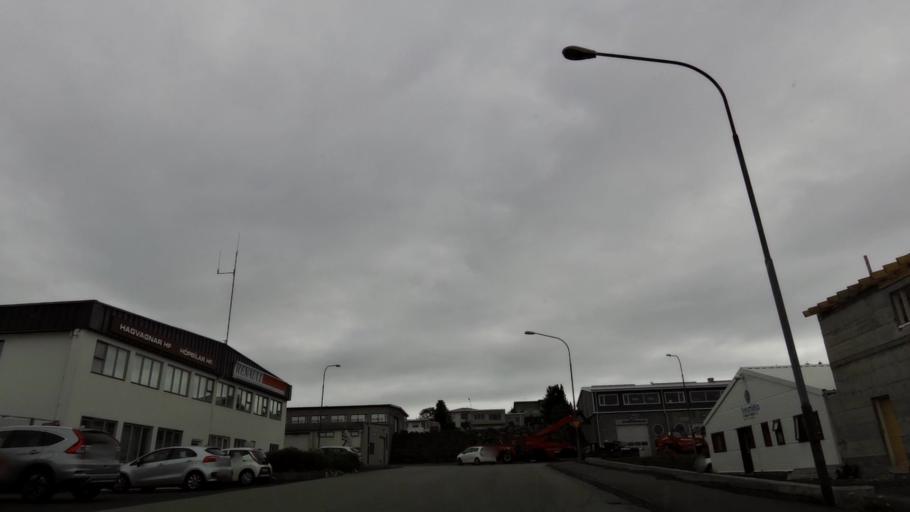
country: IS
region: Capital Region
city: Hafnarfjoerdur
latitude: 64.0590
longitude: -21.9753
